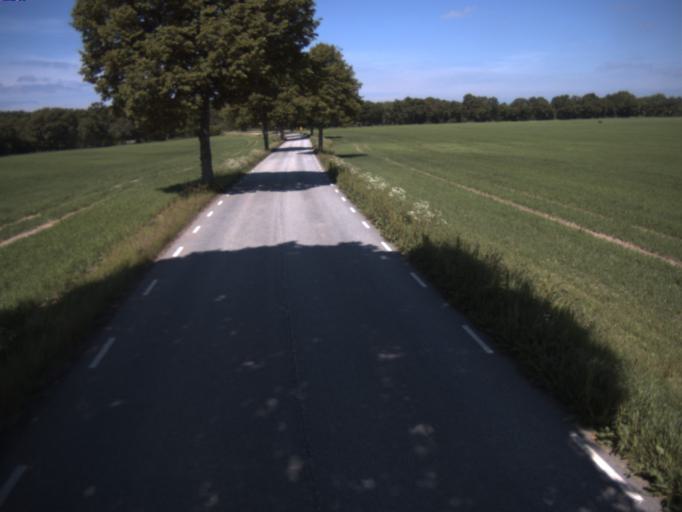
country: SE
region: Skane
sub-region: Helsingborg
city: Odakra
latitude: 56.1117
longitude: 12.6764
